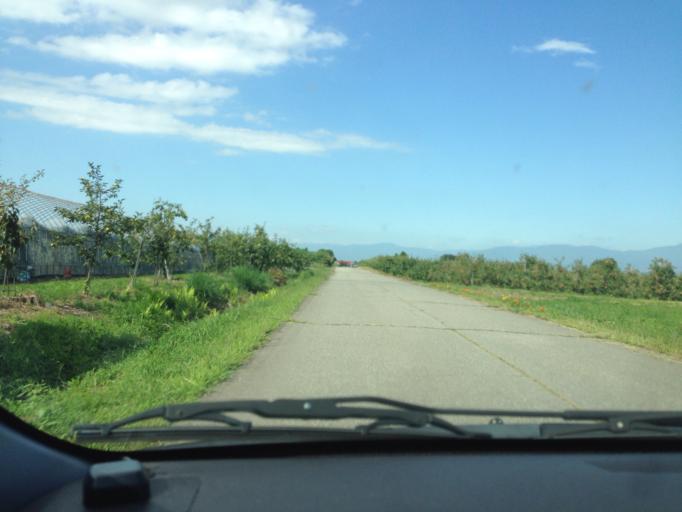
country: JP
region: Fukushima
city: Kitakata
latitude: 37.4383
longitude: 139.8099
